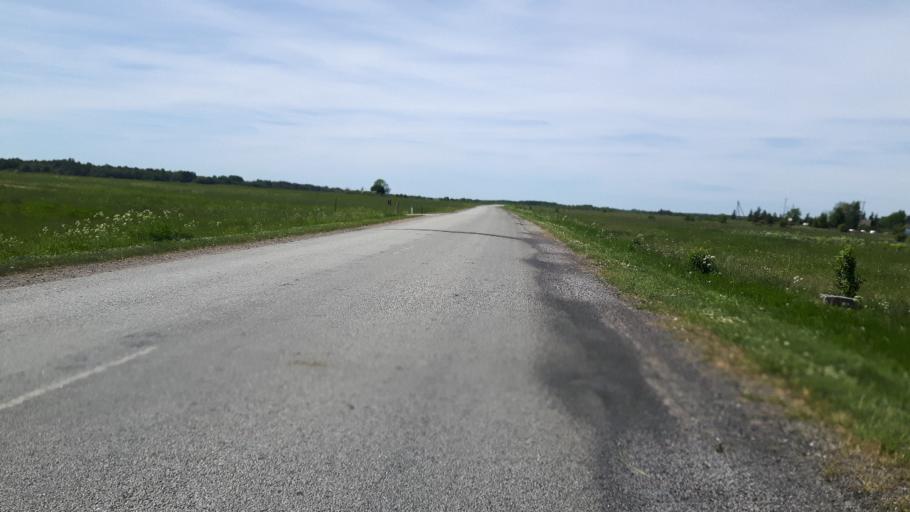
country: EE
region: Harju
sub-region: Kuusalu vald
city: Kuusalu
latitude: 59.4589
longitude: 25.3449
